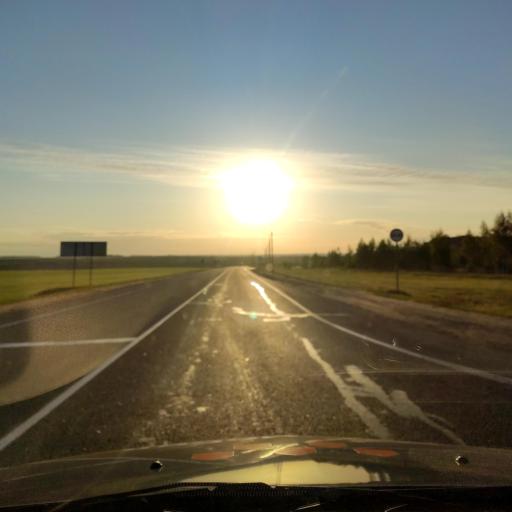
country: RU
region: Orjol
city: Livny
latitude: 52.4464
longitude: 37.5950
